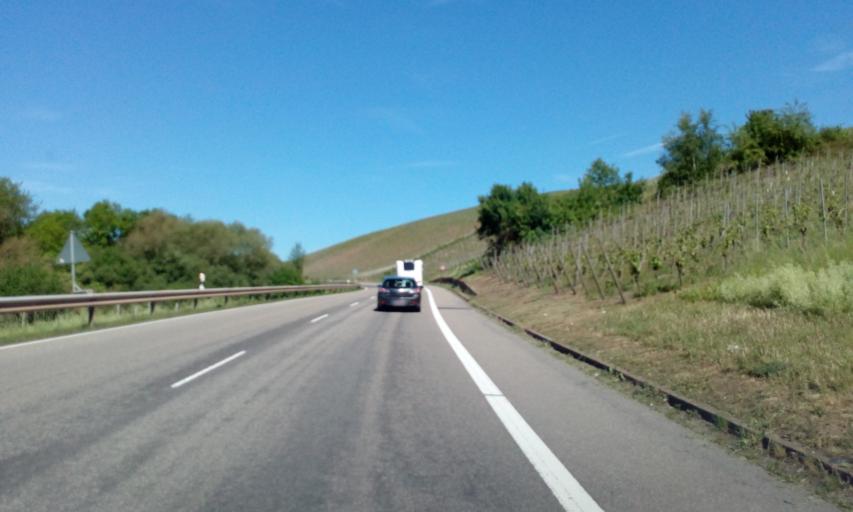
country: DE
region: Rheinland-Pfalz
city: Thornich
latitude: 49.8460
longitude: 6.8205
